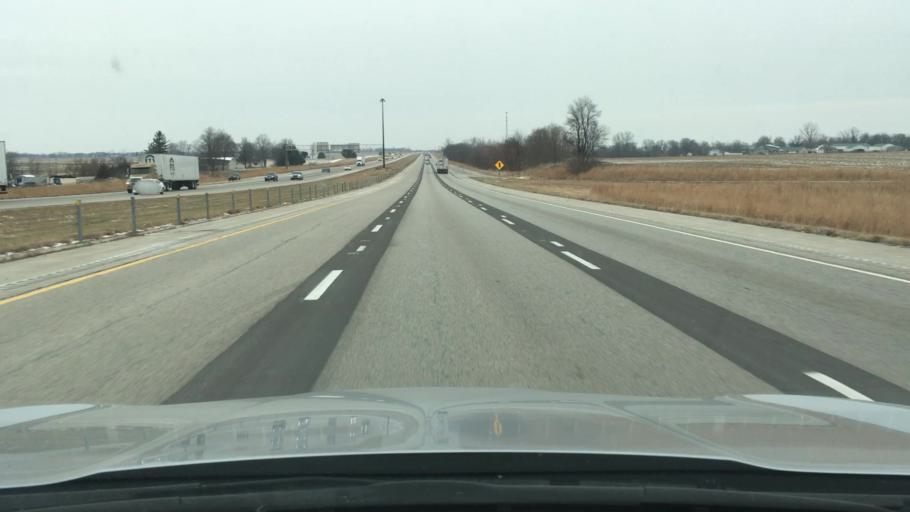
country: US
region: Illinois
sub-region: Sangamon County
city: Divernon
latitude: 39.5929
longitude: -89.6464
